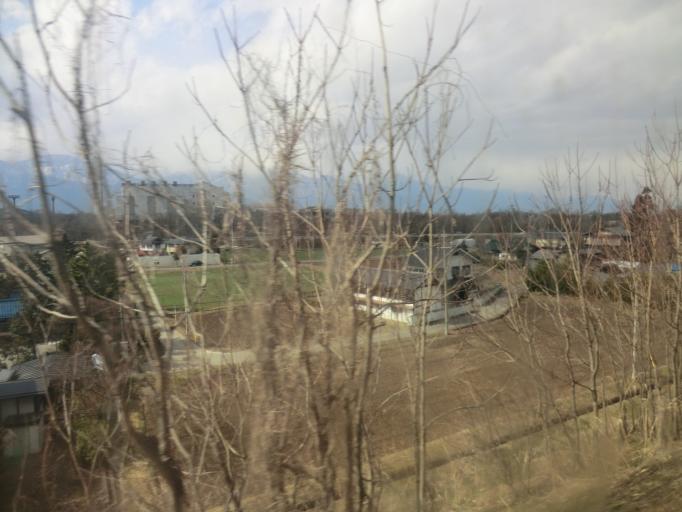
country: JP
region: Nagano
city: Matsumoto
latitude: 36.2698
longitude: 137.9477
